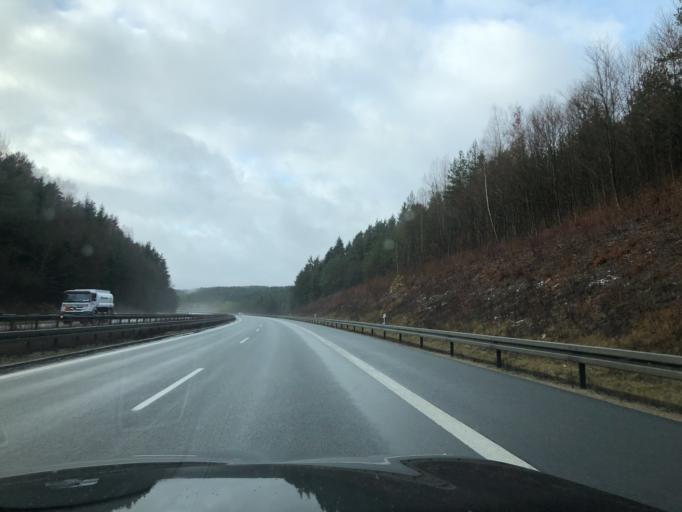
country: DE
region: Bavaria
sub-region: Upper Palatinate
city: Amberg
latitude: 49.4012
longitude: 11.8303
